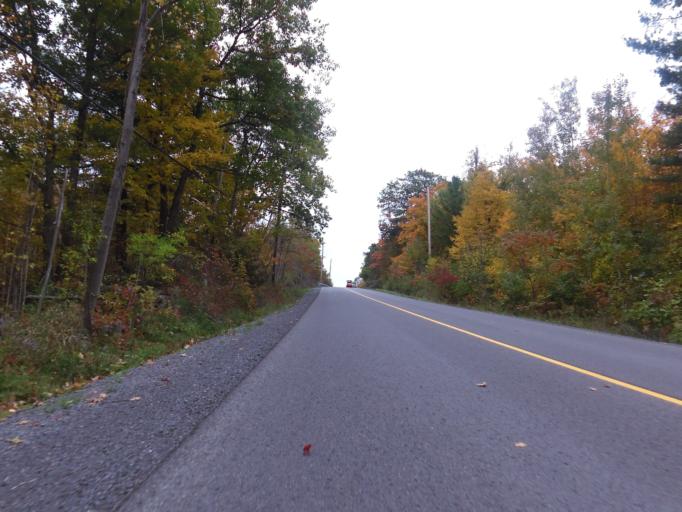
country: CA
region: Ontario
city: Arnprior
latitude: 45.4155
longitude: -76.0865
